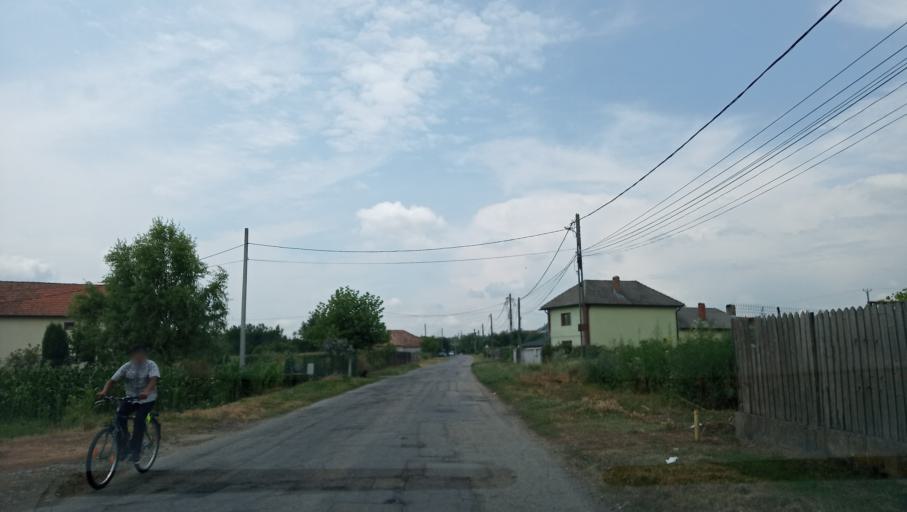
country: RO
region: Gorj
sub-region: Comuna Turcinesti
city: Turcinesti
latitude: 45.1158
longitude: 23.3261
